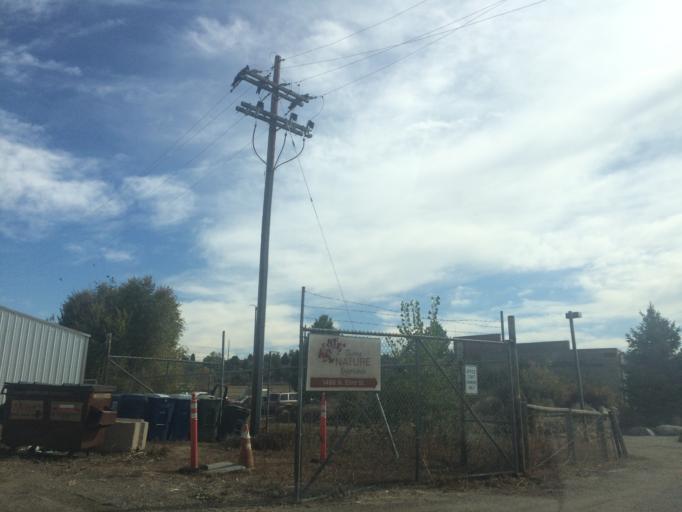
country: US
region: Colorado
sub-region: Boulder County
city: Gunbarrel
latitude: 40.0123
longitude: -105.2027
